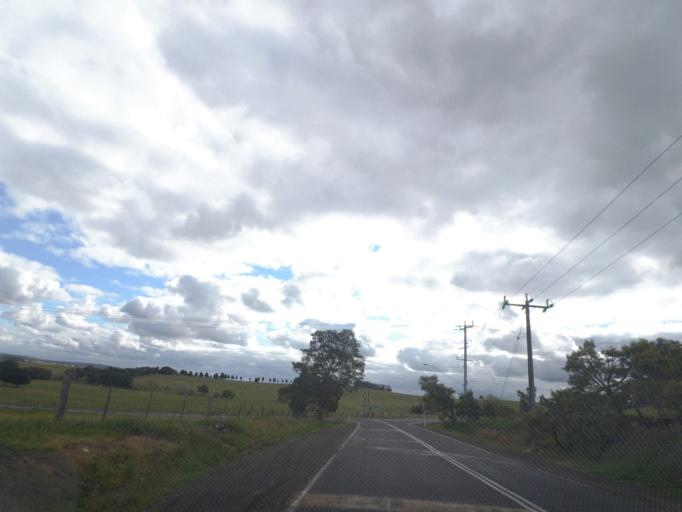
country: AU
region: Victoria
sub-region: Whittlesea
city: Whittlesea
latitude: -37.5193
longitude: 145.0278
